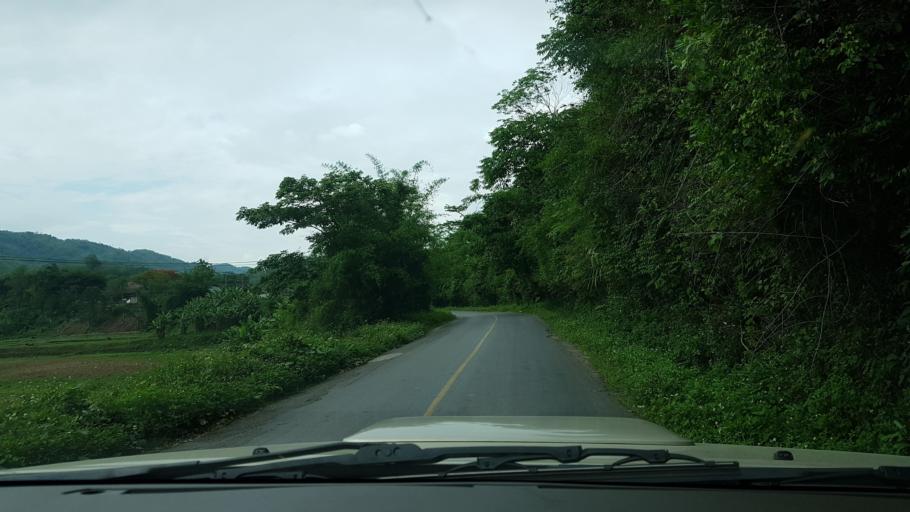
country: LA
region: Loungnamtha
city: Muang Nale
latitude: 20.3791
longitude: 101.7403
